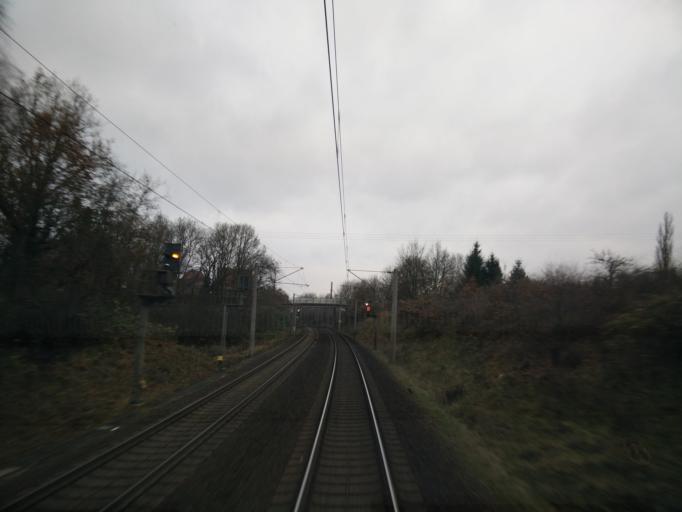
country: DE
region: Mecklenburg-Vorpommern
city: Ludwigslust
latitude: 53.3255
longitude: 11.5060
